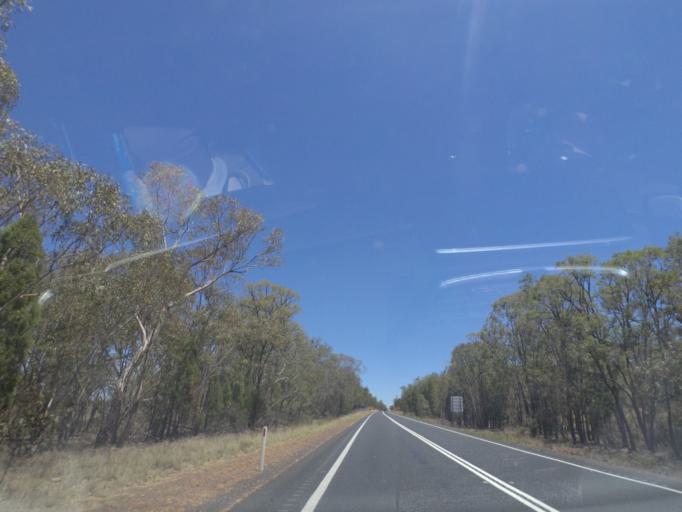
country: AU
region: New South Wales
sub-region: Warrumbungle Shire
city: Coonabarabran
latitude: -31.2271
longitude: 149.3217
